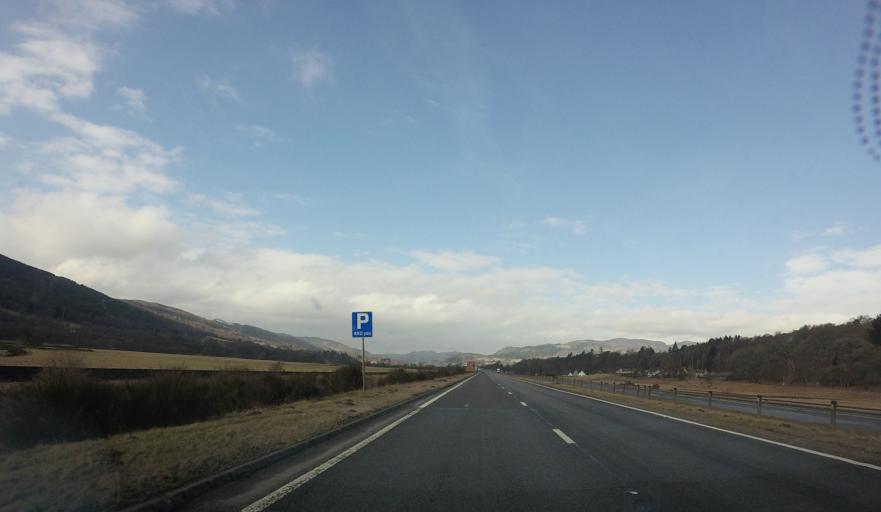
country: GB
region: Scotland
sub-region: Perth and Kinross
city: Pitlochry
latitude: 56.6809
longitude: -3.6939
